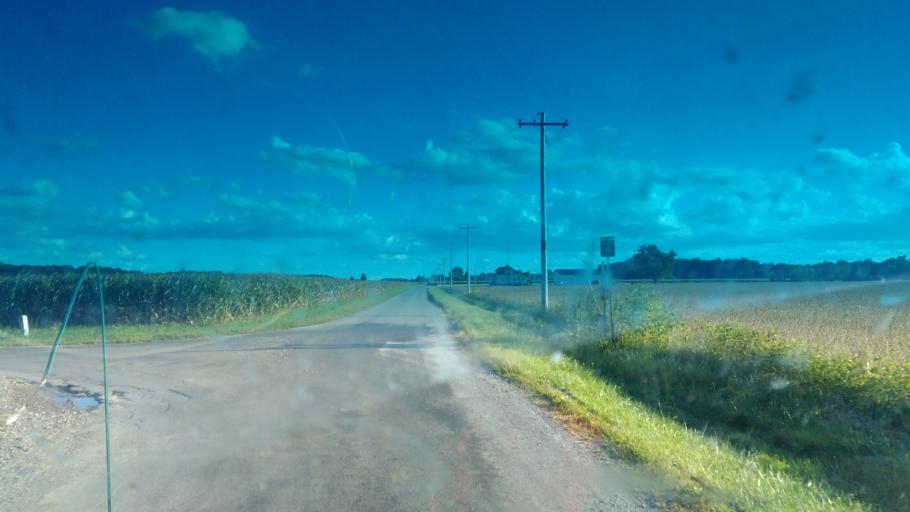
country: US
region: Ohio
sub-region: Wyandot County
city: Carey
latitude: 40.9015
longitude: -83.3572
